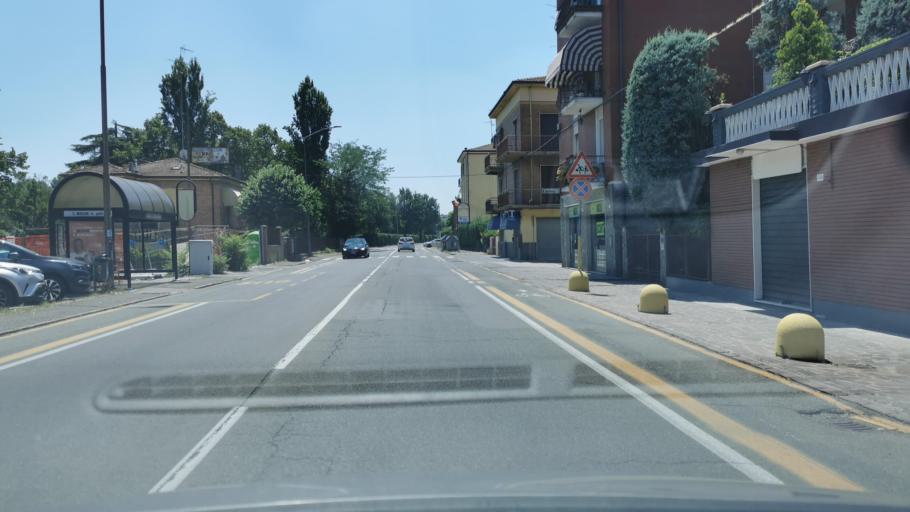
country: IT
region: Emilia-Romagna
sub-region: Provincia di Modena
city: Modena
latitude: 44.6302
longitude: 10.9266
